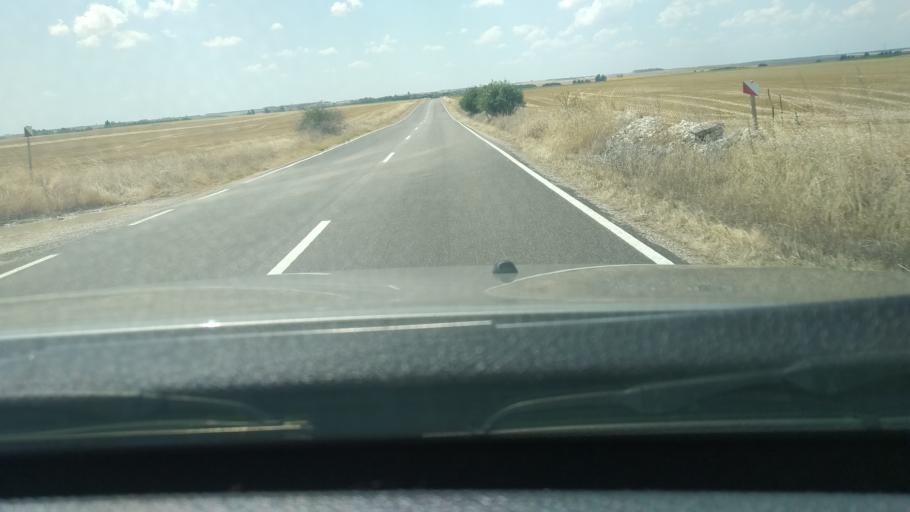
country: ES
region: Castille and Leon
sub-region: Provincia de Burgos
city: Villafruela
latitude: 41.9262
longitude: -3.8958
